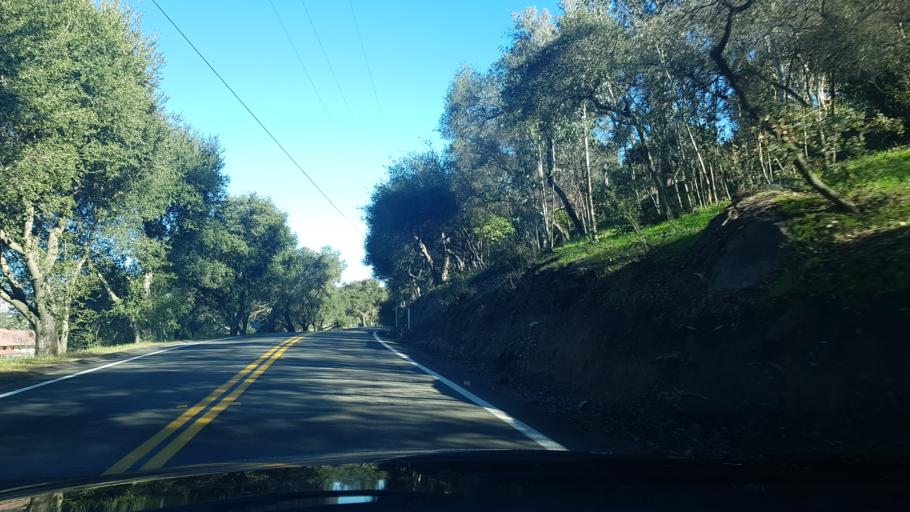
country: US
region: California
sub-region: San Diego County
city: Valley Center
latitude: 33.2056
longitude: -116.9817
